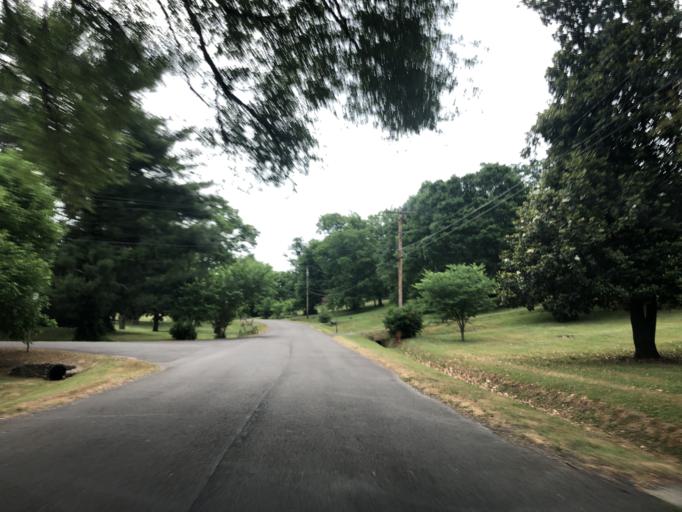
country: US
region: Tennessee
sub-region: Davidson County
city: Goodlettsville
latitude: 36.2642
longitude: -86.7731
